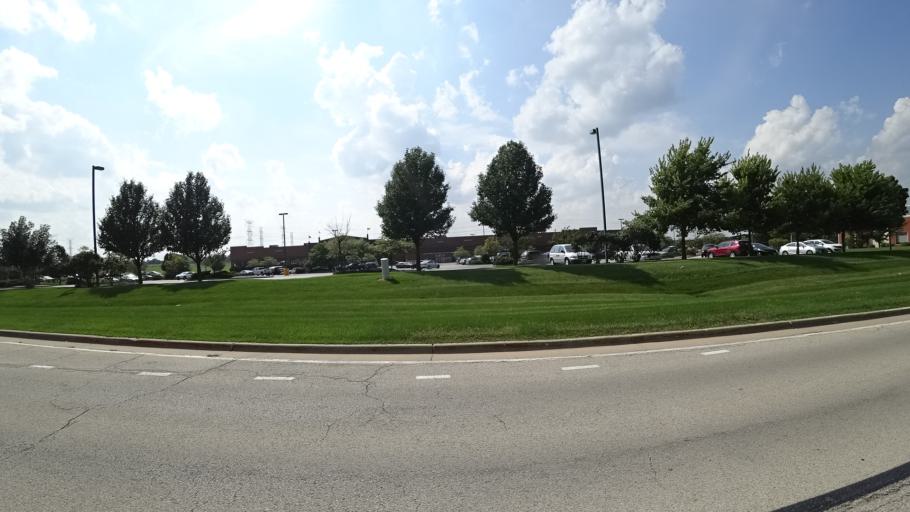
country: US
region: Illinois
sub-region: Will County
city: Goodings Grove
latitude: 41.6350
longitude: -87.9313
